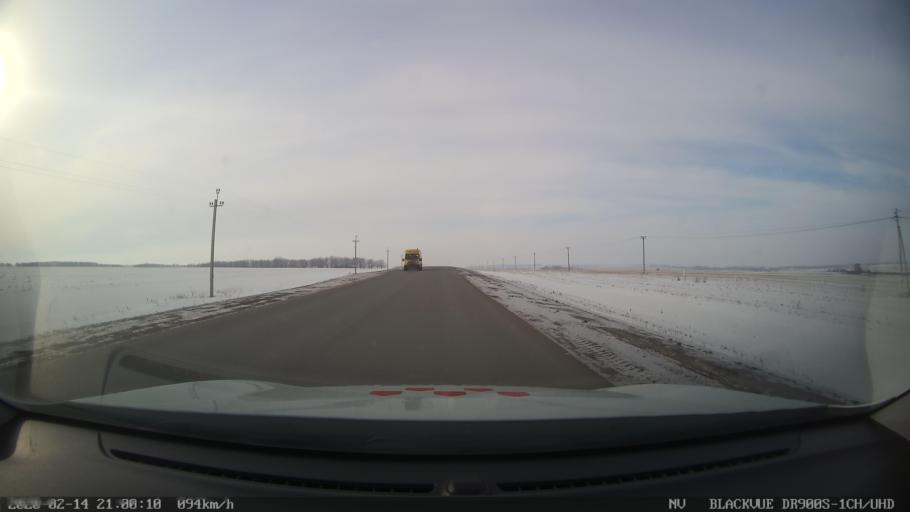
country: RU
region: Tatarstan
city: Kuybyshevskiy Zaton
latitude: 55.1731
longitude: 49.2254
